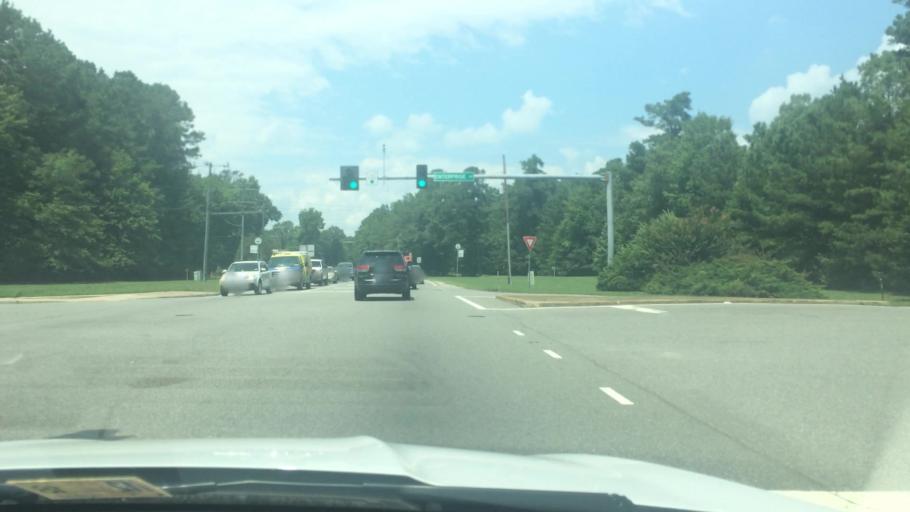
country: US
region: Virginia
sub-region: York County
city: Yorktown
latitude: 37.1808
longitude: -76.5700
